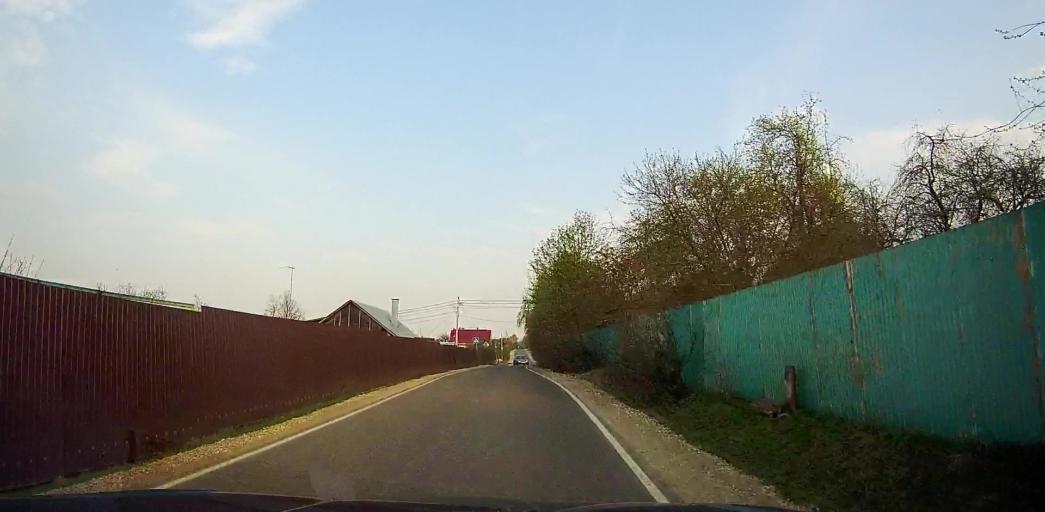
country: RU
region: Moskovskaya
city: Andreyevskoye
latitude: 55.5572
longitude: 37.9192
